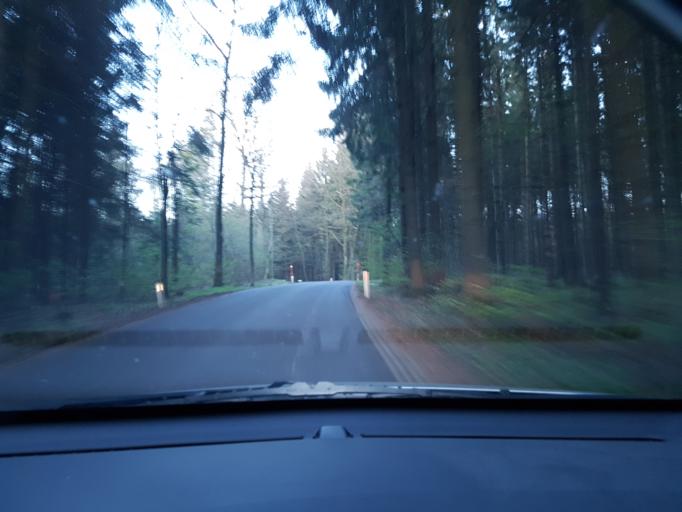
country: AT
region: Upper Austria
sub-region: Politischer Bezirk Linz-Land
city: Ansfelden
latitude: 48.1983
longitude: 14.3244
